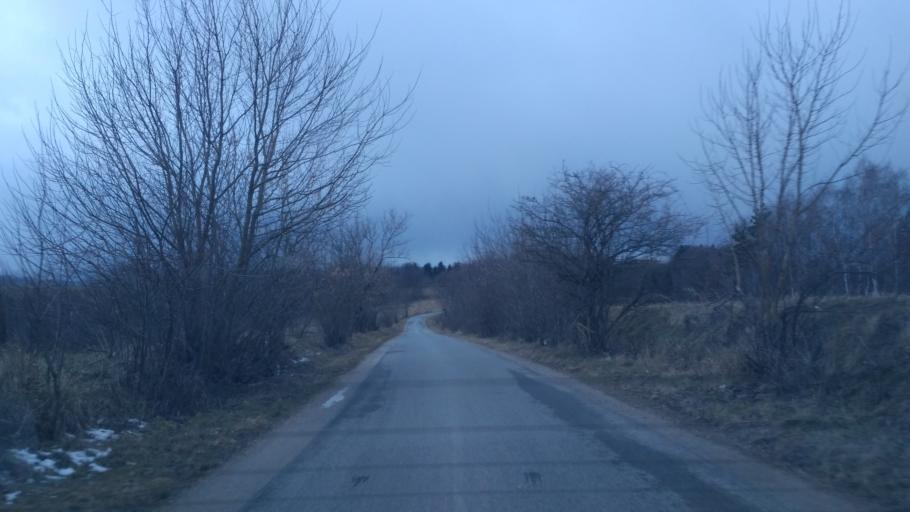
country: PL
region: Subcarpathian Voivodeship
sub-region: Powiat rzeszowski
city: Blazowa
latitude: 49.8893
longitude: 22.1424
